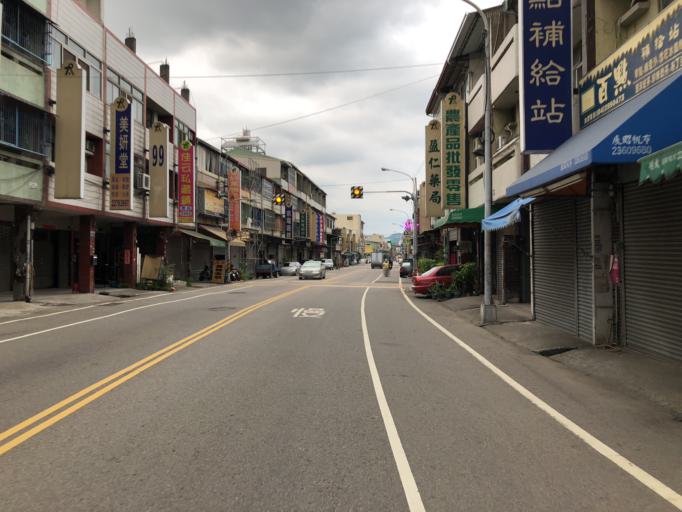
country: TW
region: Taiwan
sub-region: Taichung City
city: Taichung
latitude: 24.1076
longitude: 120.7294
